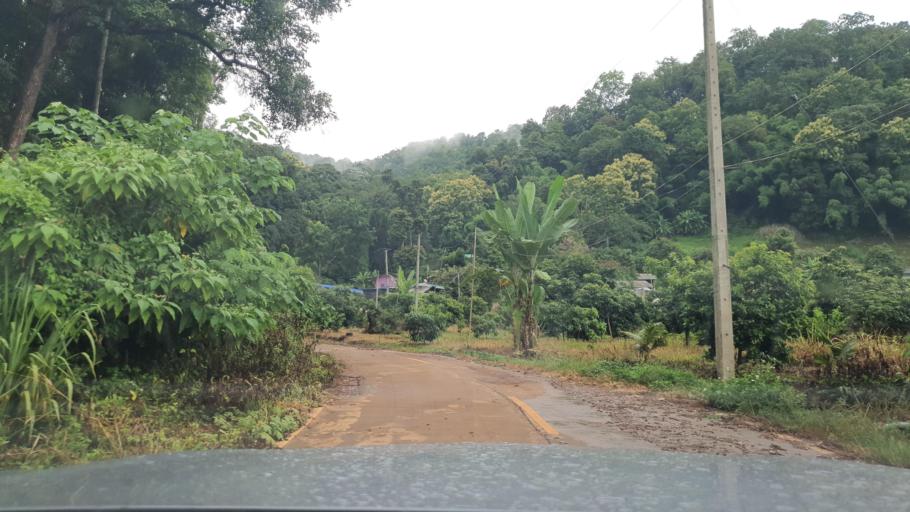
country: TH
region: Chiang Mai
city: Samoeng
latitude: 18.8311
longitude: 98.7736
